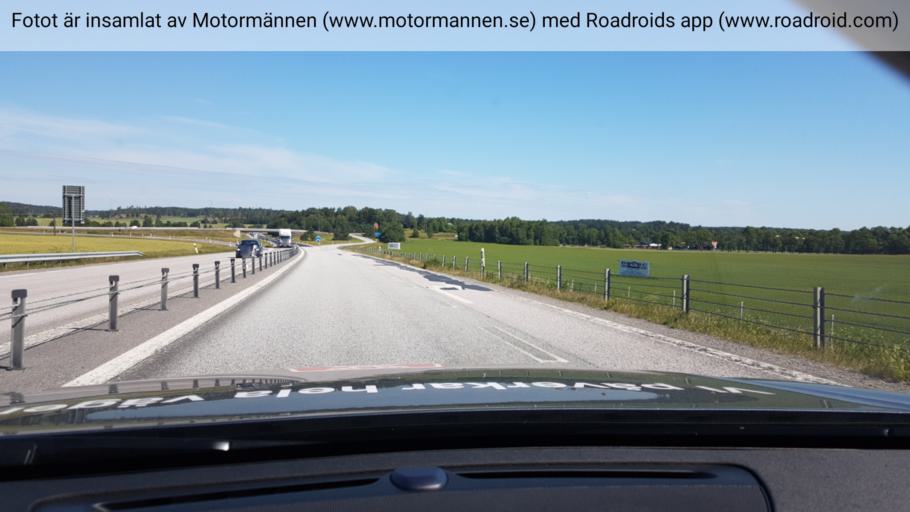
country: SE
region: Stockholm
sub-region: Osterakers Kommun
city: Akersberga
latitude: 59.5552
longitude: 18.2307
